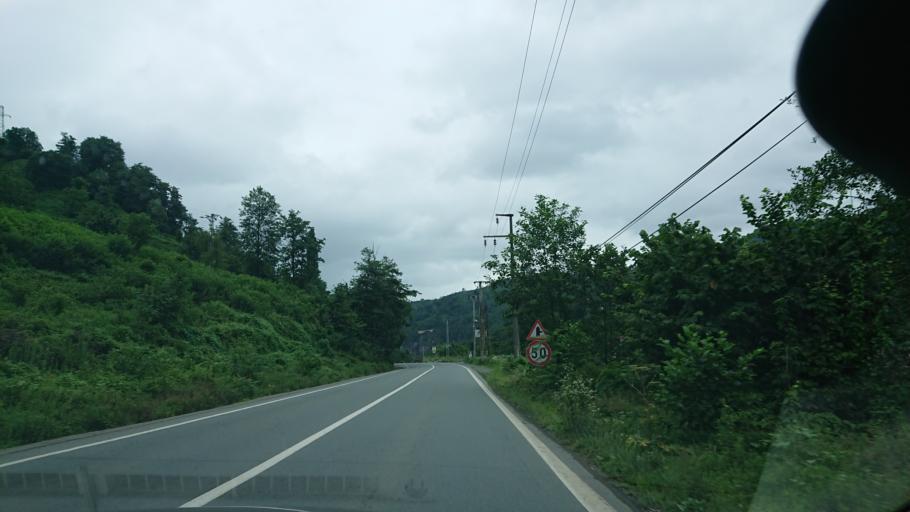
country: TR
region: Rize
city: Gundogdu
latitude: 41.0192
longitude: 40.5733
